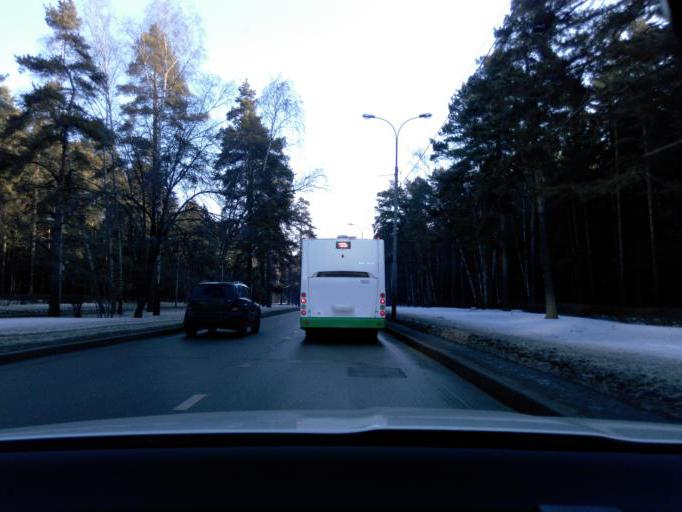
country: RU
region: Moskovskaya
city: Rzhavki
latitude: 55.9936
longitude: 37.2284
